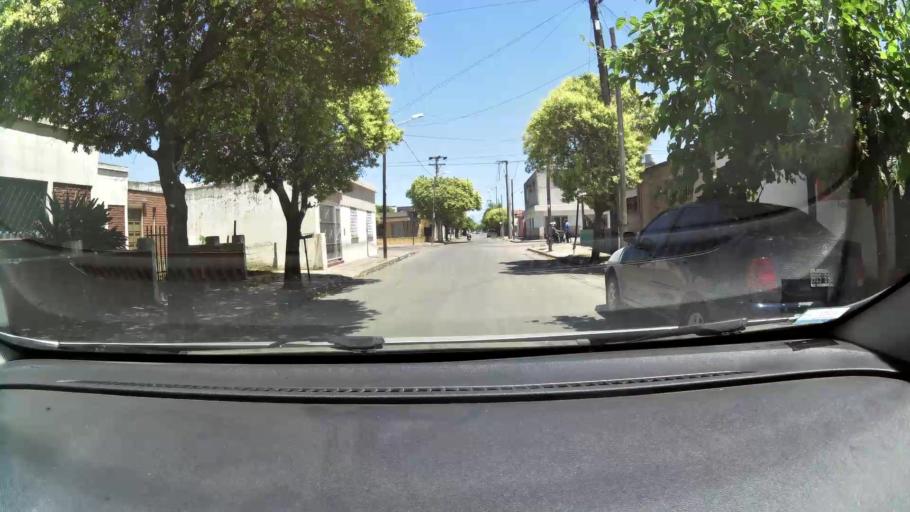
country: AR
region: Cordoba
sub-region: Departamento de Capital
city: Cordoba
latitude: -31.4247
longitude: -64.1230
